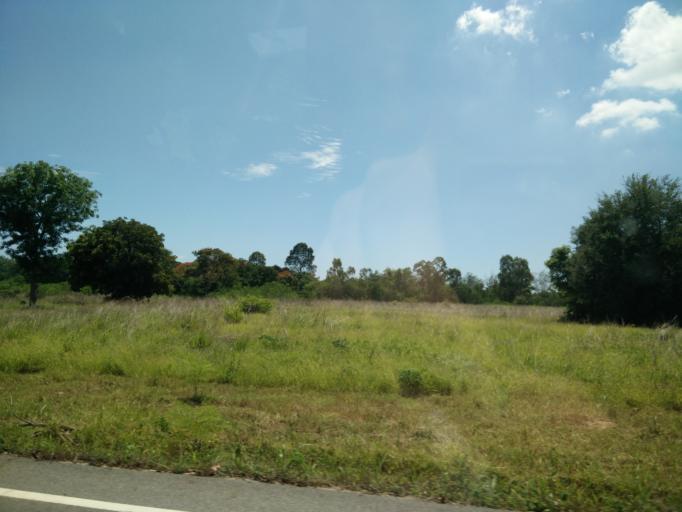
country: TH
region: Chon Buri
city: Phatthaya
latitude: 12.9070
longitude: 100.9892
